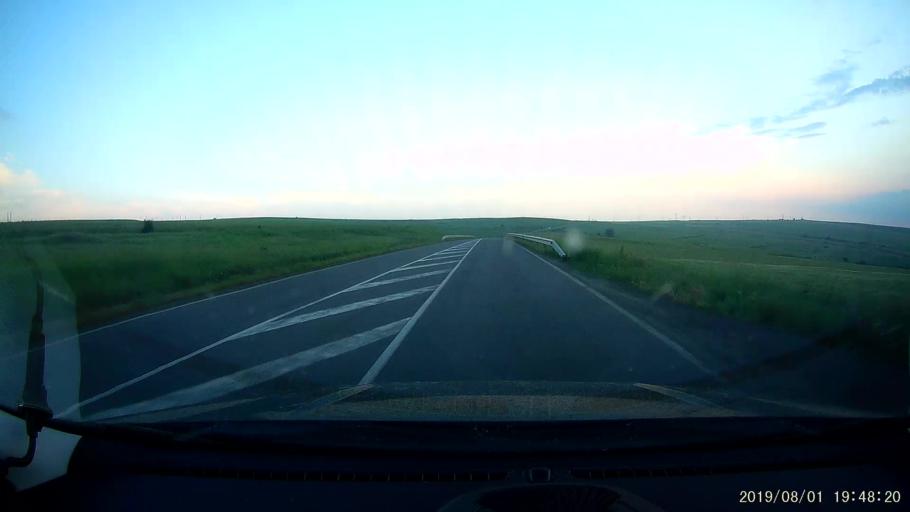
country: BG
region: Burgas
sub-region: Obshtina Karnobat
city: Karnobat
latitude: 42.6388
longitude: 26.9511
